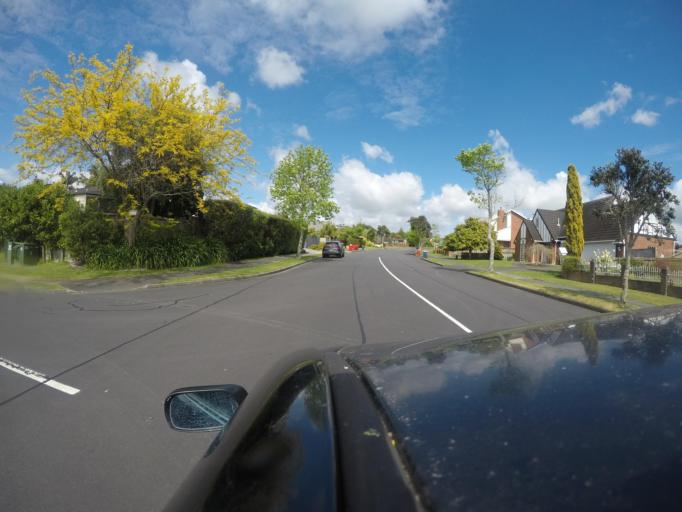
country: NZ
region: Auckland
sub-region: Auckland
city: Rosebank
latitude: -36.8177
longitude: 174.6380
